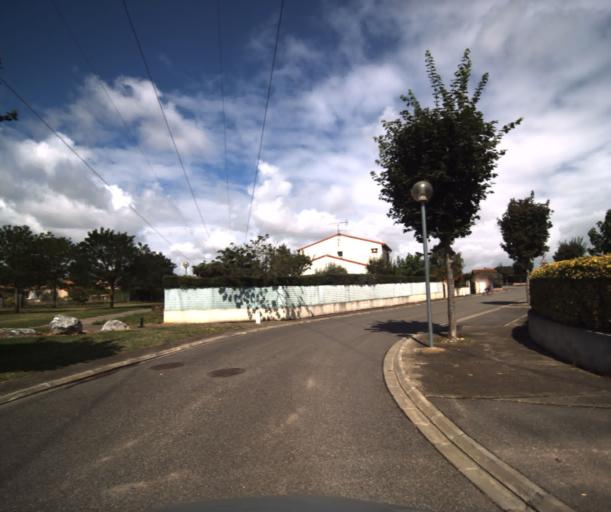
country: FR
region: Midi-Pyrenees
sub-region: Departement de la Haute-Garonne
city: Portet-sur-Garonne
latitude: 43.5163
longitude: 1.3989
